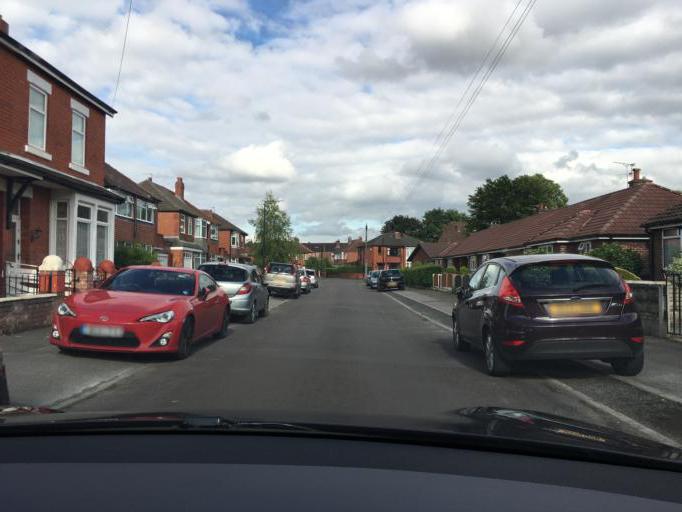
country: GB
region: England
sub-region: Trafford
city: Urmston
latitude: 53.4504
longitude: -2.3494
